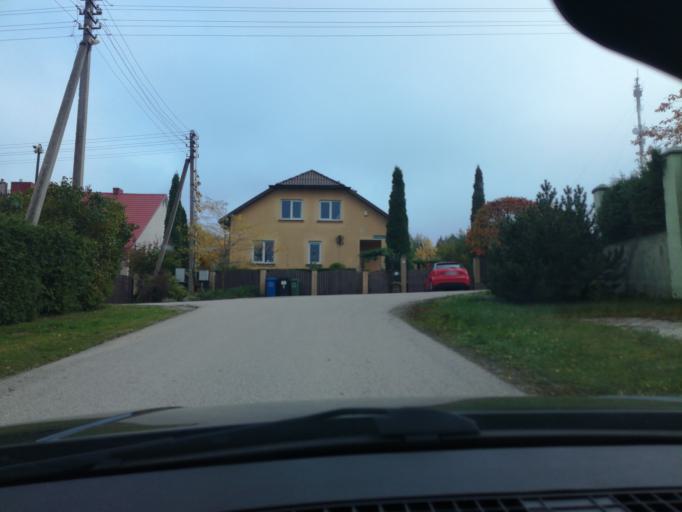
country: LT
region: Alytaus apskritis
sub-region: Alytus
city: Alytus
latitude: 54.3988
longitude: 24.0025
